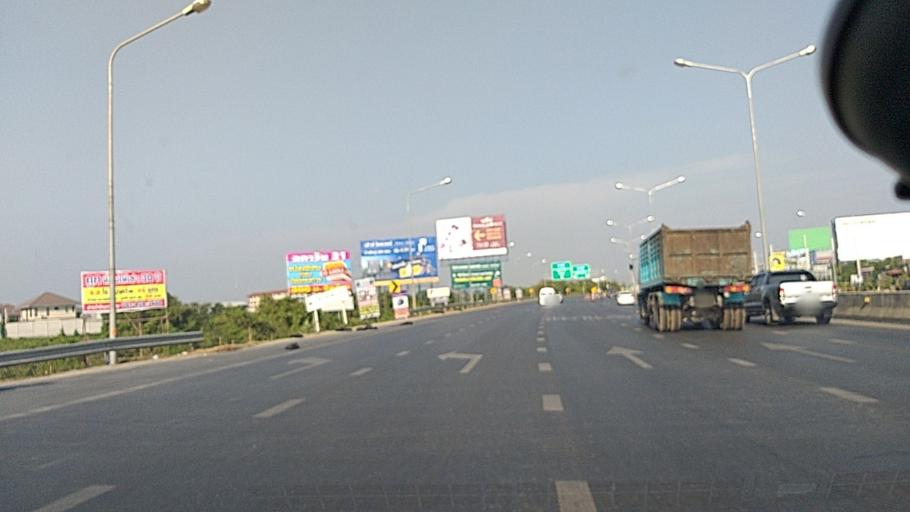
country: TH
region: Nonthaburi
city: Bang Bua Thong
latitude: 13.9294
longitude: 100.4438
